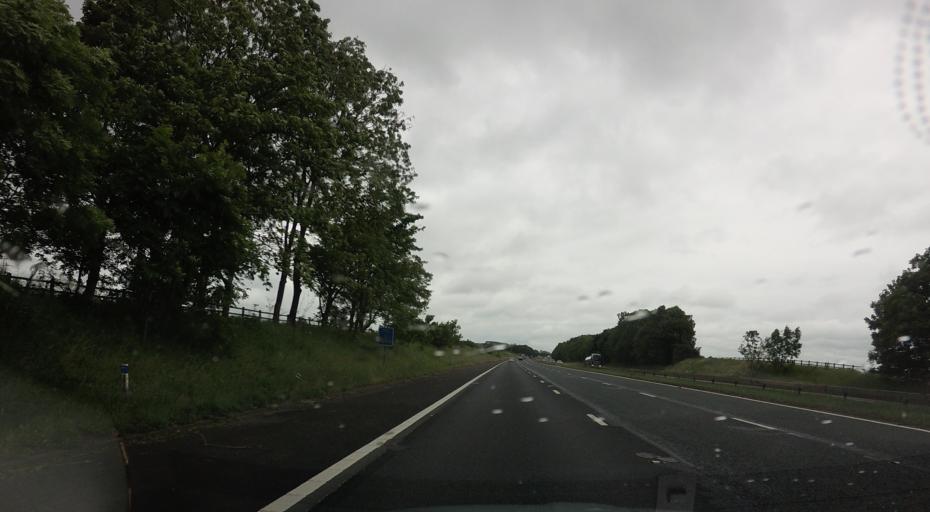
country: GB
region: England
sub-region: Cumbria
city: Penrith
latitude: 54.7149
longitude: -2.7968
